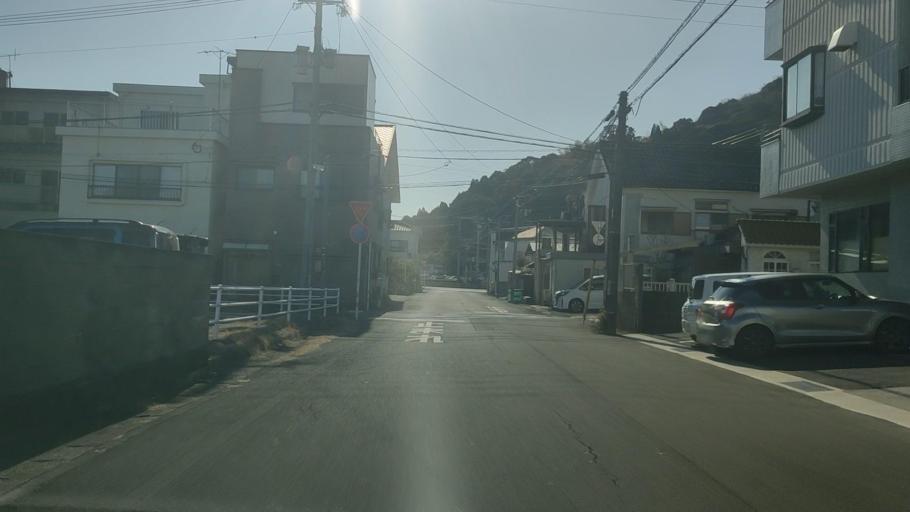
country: JP
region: Oita
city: Saiki
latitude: 32.9718
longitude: 131.9034
